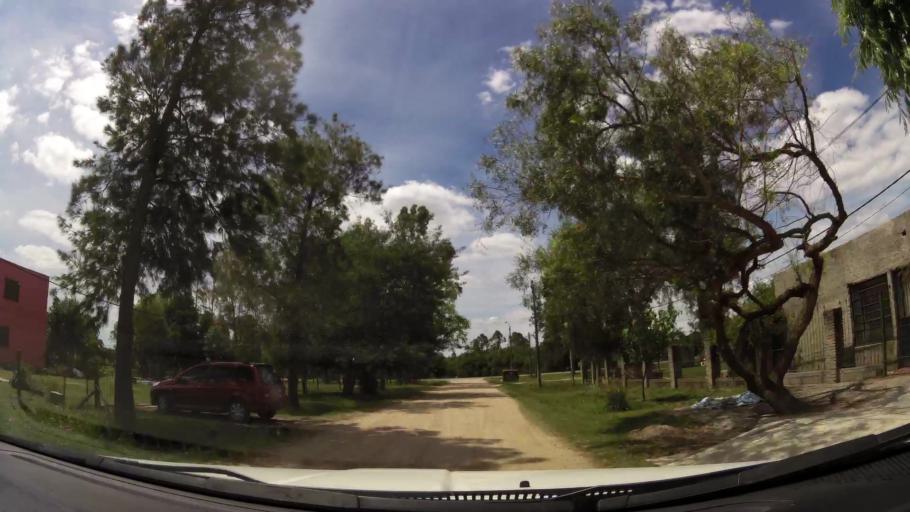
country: UY
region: San Jose
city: Delta del Tigre
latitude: -34.7410
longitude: -56.4371
